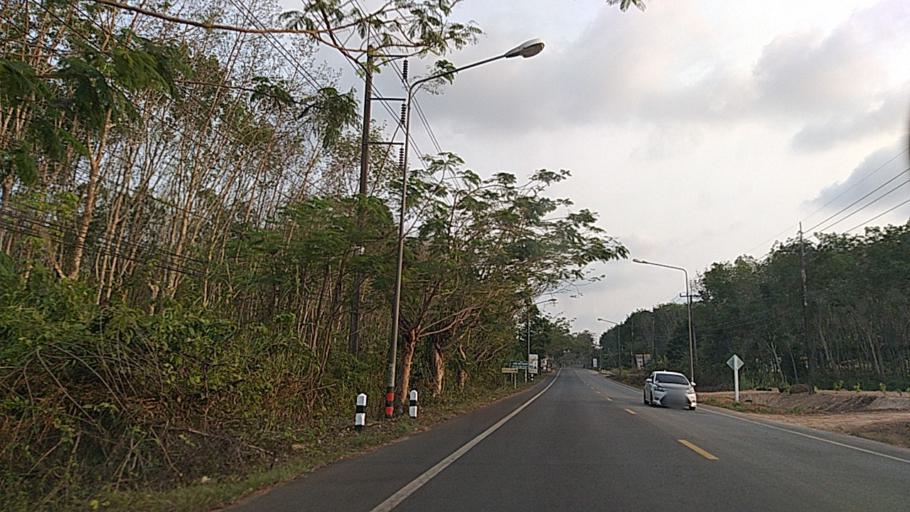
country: TH
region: Trat
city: Laem Ngop
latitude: 12.2732
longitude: 102.3057
